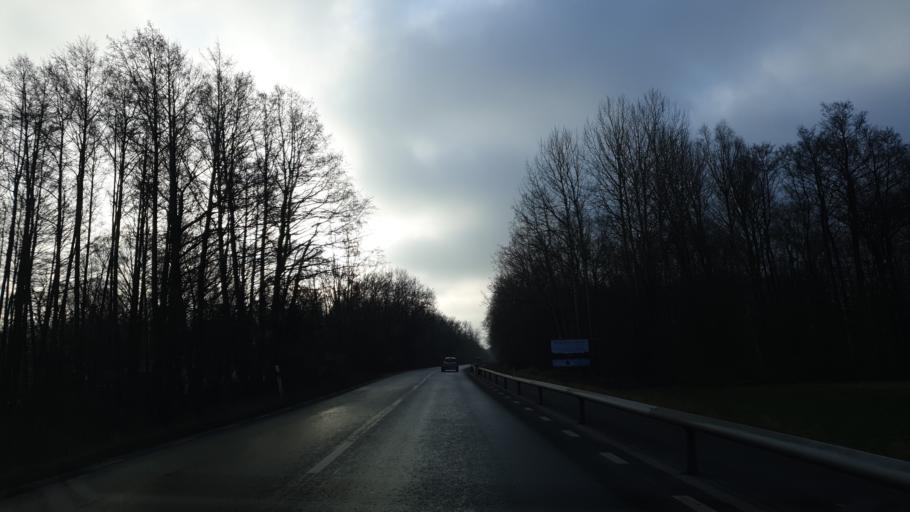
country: SE
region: Blekinge
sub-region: Karlshamns Kommun
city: Morrum
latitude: 56.1333
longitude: 14.6725
